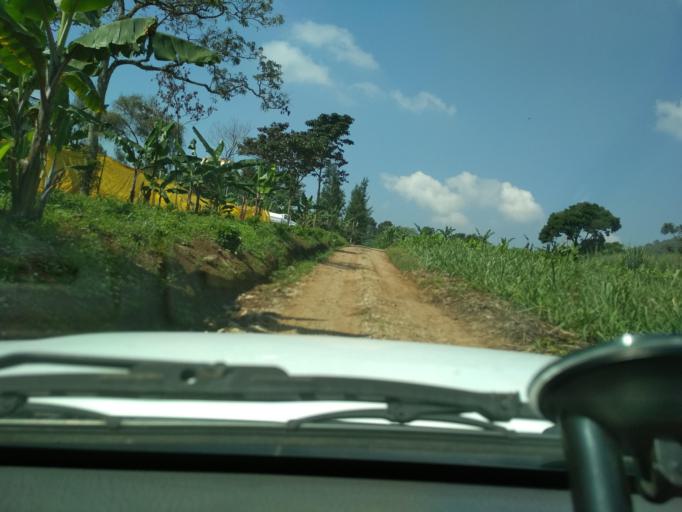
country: MX
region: Veracruz
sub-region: Fortin
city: Santa Lucia Potrerillo
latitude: 18.9803
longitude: -97.0185
